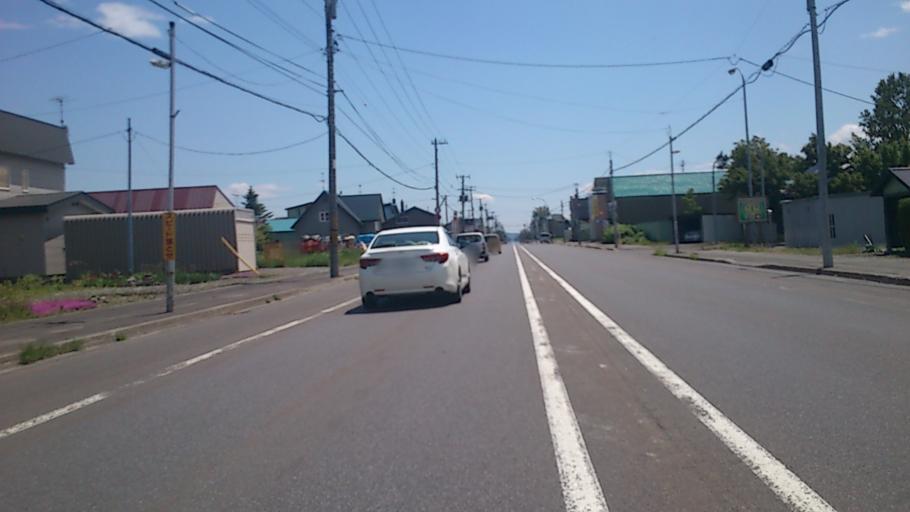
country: JP
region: Hokkaido
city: Nayoro
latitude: 44.2439
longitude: 142.3949
